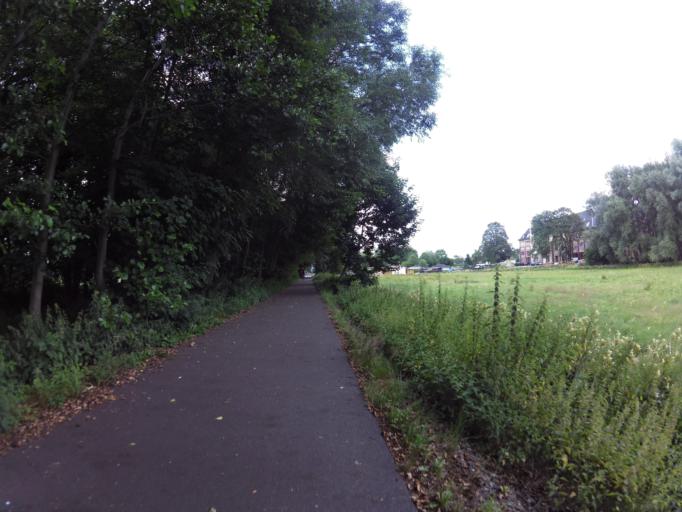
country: DE
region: Thuringia
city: Schleiz
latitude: 50.5778
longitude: 11.8017
